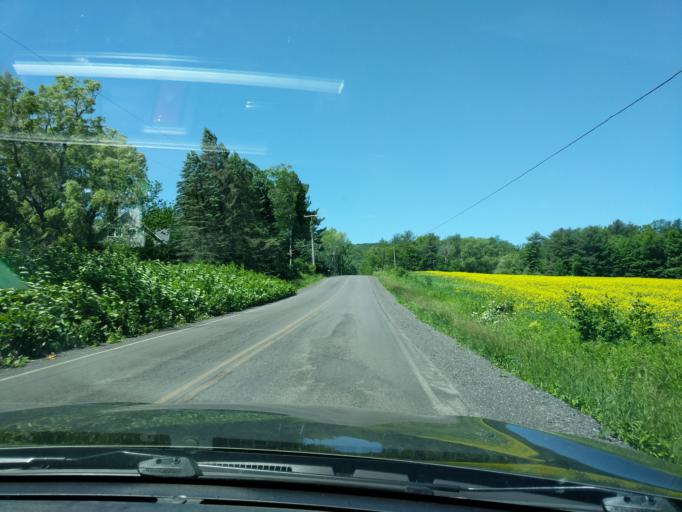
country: US
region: New York
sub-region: Tompkins County
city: East Ithaca
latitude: 42.3699
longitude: -76.4051
